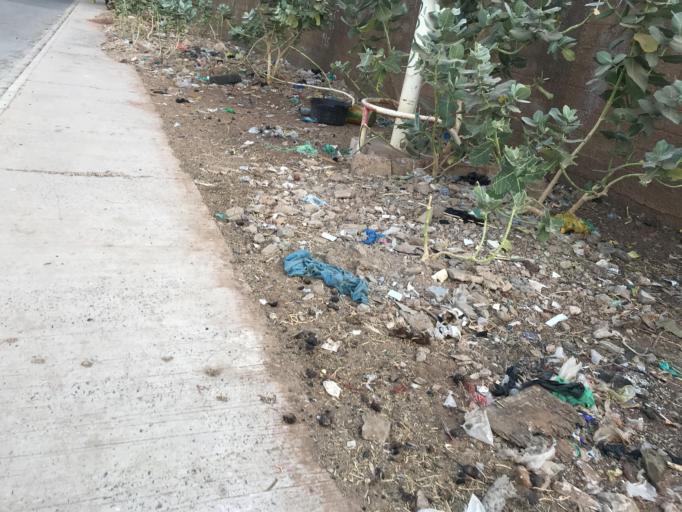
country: SN
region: Louga
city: Ndibene Dahra
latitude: 15.3999
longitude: -15.1157
